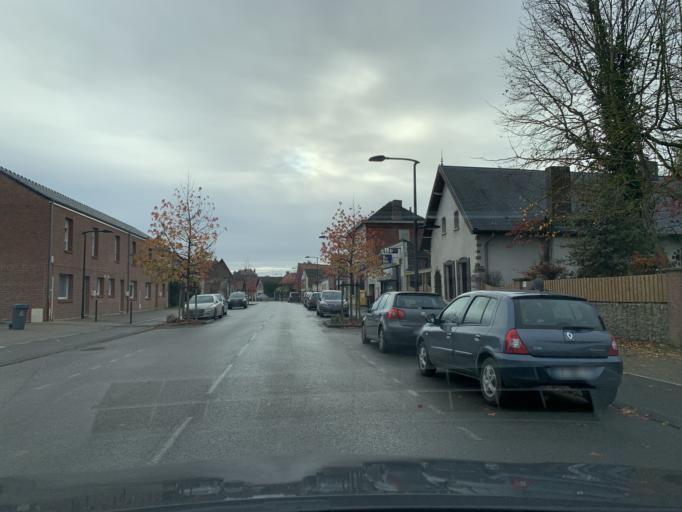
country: FR
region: Nord-Pas-de-Calais
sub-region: Departement du Nord
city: Cantin
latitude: 50.3124
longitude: 3.1234
